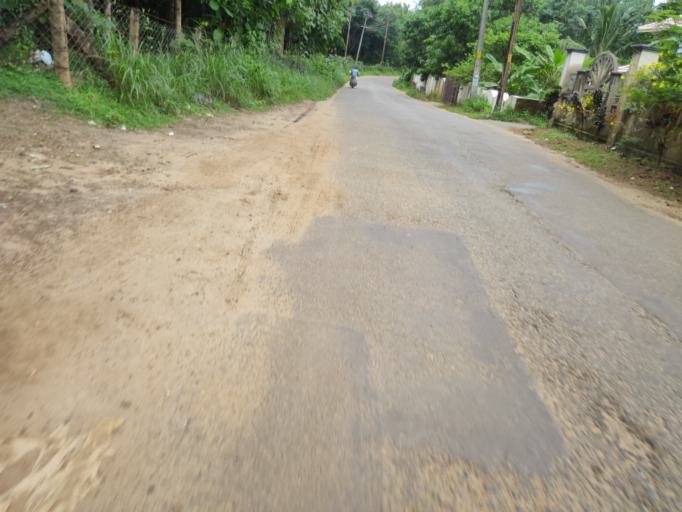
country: IN
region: Kerala
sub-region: Malappuram
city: Manjeri
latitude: 11.2408
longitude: 76.2869
